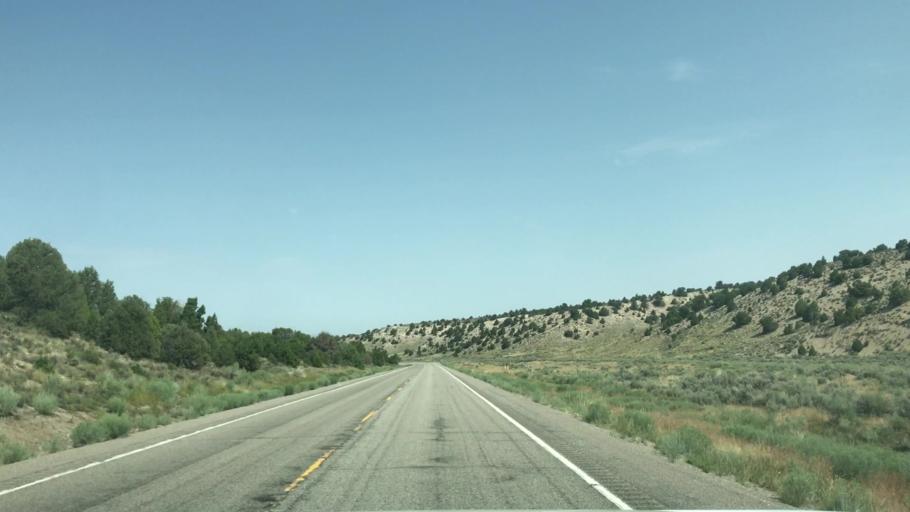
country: US
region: Nevada
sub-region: White Pine County
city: Ely
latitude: 39.0254
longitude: -114.6906
